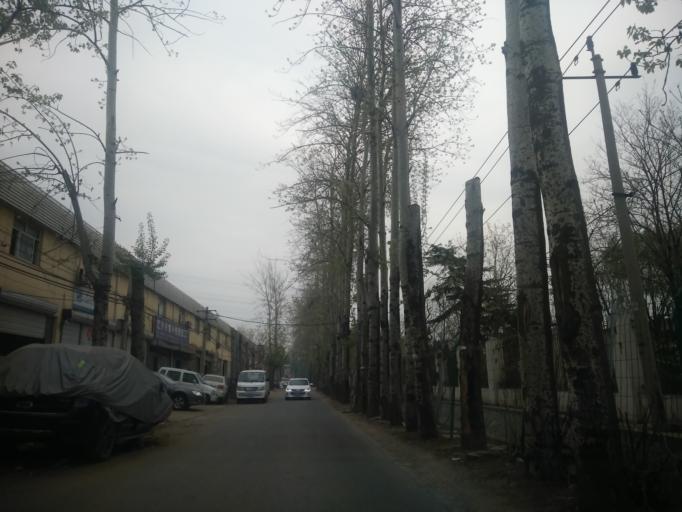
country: CN
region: Beijing
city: Jiugong
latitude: 39.8129
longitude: 116.4746
